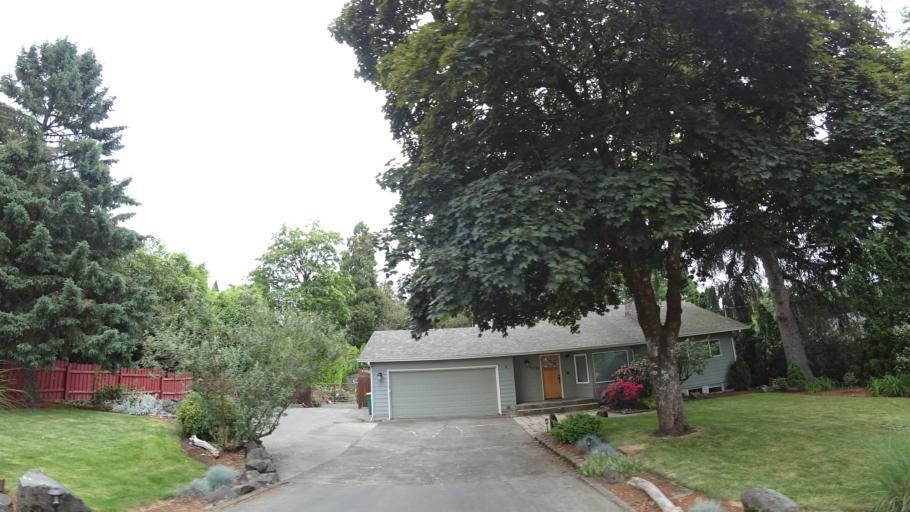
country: US
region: Oregon
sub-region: Washington County
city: Garden Home-Whitford
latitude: 45.4637
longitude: -122.7611
